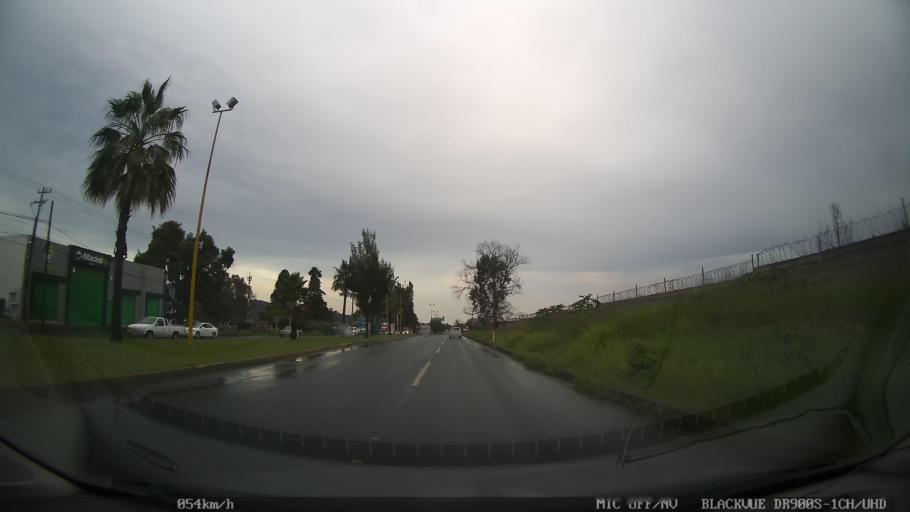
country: MX
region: Michoacan
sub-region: Uruapan
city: Santa Rosa (Santa Barbara)
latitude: 19.3850
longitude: -102.0433
